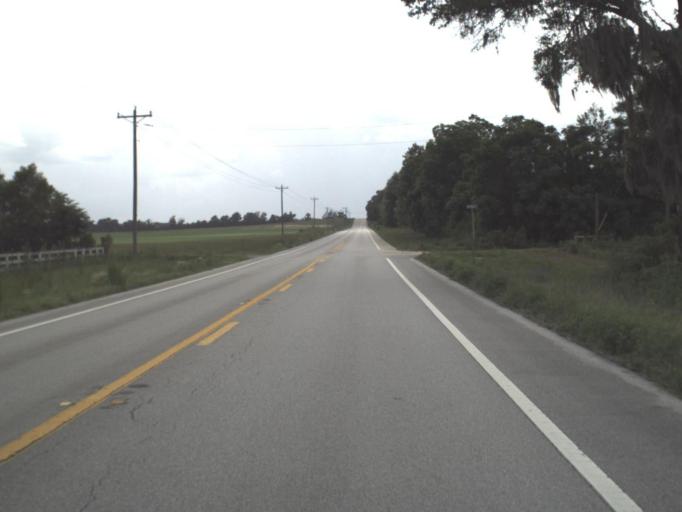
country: US
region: Florida
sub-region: Madison County
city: Madison
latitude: 30.4723
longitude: -83.3162
